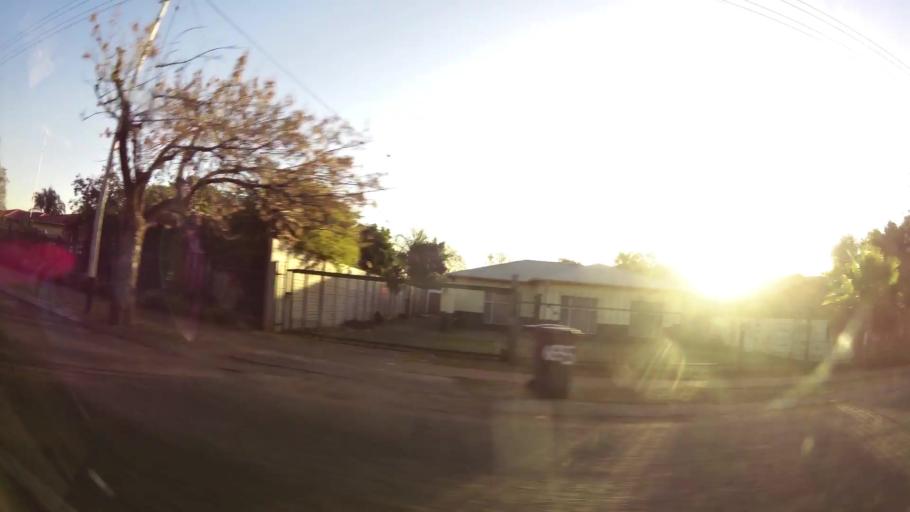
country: ZA
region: Gauteng
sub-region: City of Tshwane Metropolitan Municipality
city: Pretoria
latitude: -25.7092
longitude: 28.2361
